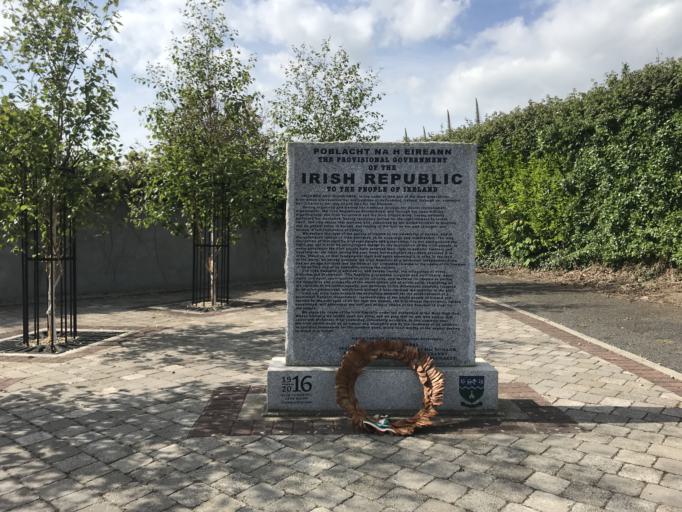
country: IE
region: Leinster
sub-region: Wicklow
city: Greystones
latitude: 53.1424
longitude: -6.0600
